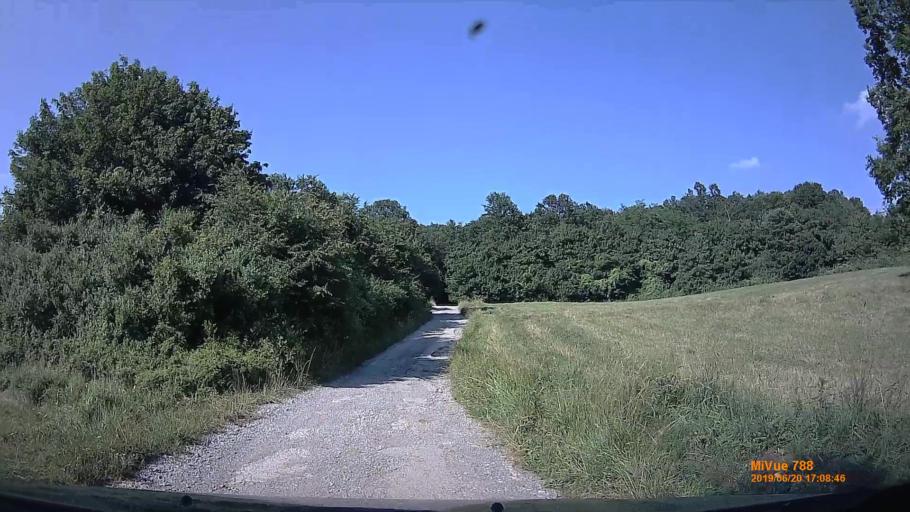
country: HU
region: Baranya
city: Buekkoesd
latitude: 46.1412
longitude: 18.0072
